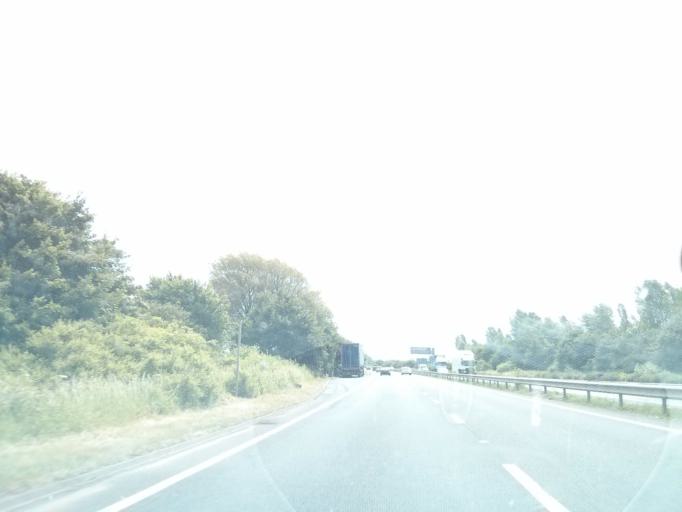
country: GB
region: England
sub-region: Leicestershire
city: Lutterworth
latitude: 52.3972
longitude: -1.1531
